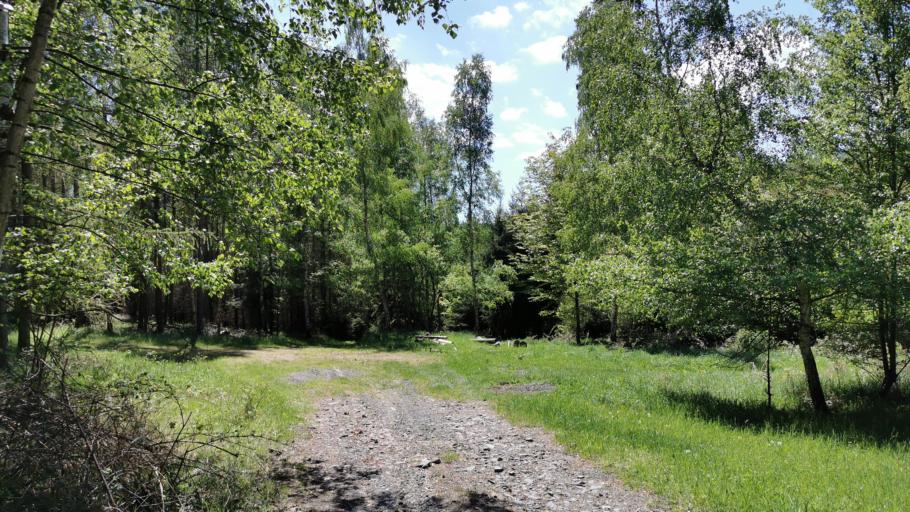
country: DE
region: Thuringia
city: Essbach
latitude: 50.5732
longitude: 11.6969
